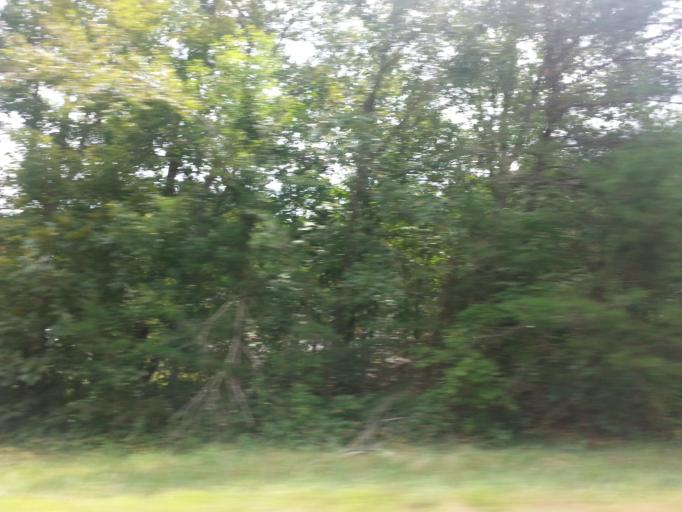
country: US
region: Tennessee
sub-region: Roane County
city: Rockwood
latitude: 35.8881
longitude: -84.8044
